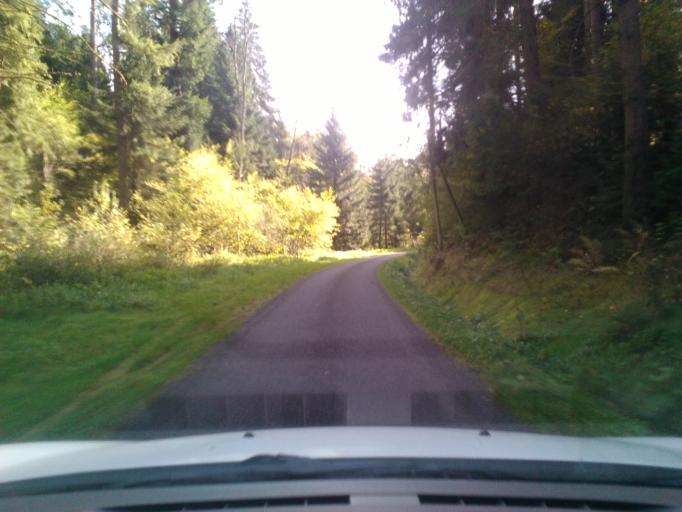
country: FR
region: Lorraine
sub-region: Departement des Vosges
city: Ban-de-Laveline
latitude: 48.3004
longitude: 7.0562
